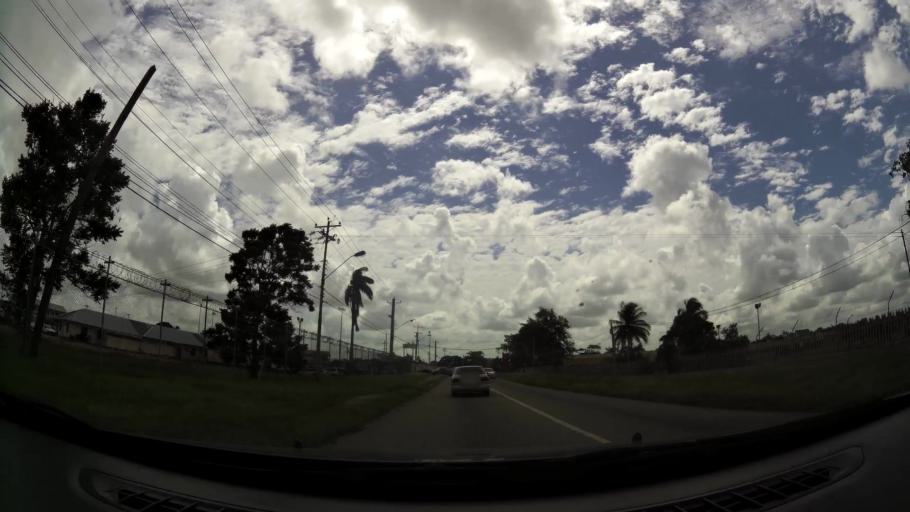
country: TT
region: City of San Fernando
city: Marabella
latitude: 10.3125
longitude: -61.4531
